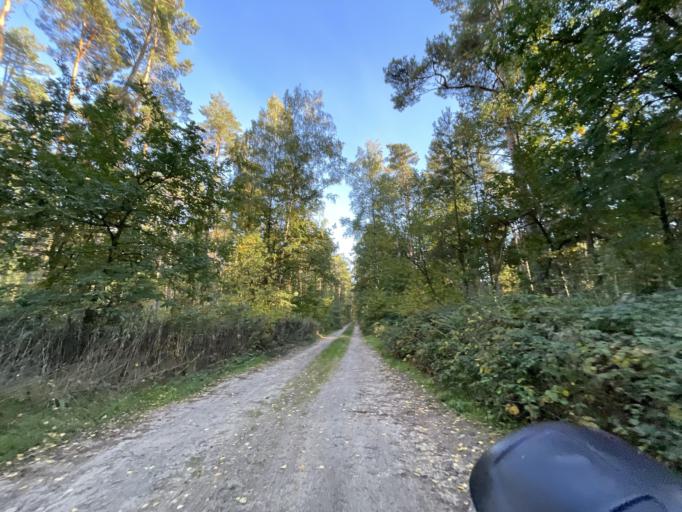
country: DE
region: Lower Saxony
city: Vastorf
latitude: 53.1923
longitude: 10.5330
